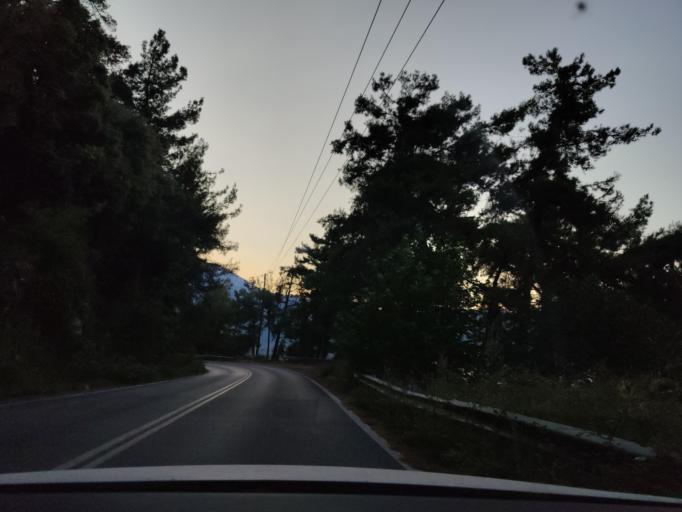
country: GR
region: East Macedonia and Thrace
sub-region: Nomos Kavalas
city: Potamia
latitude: 40.7079
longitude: 24.7653
